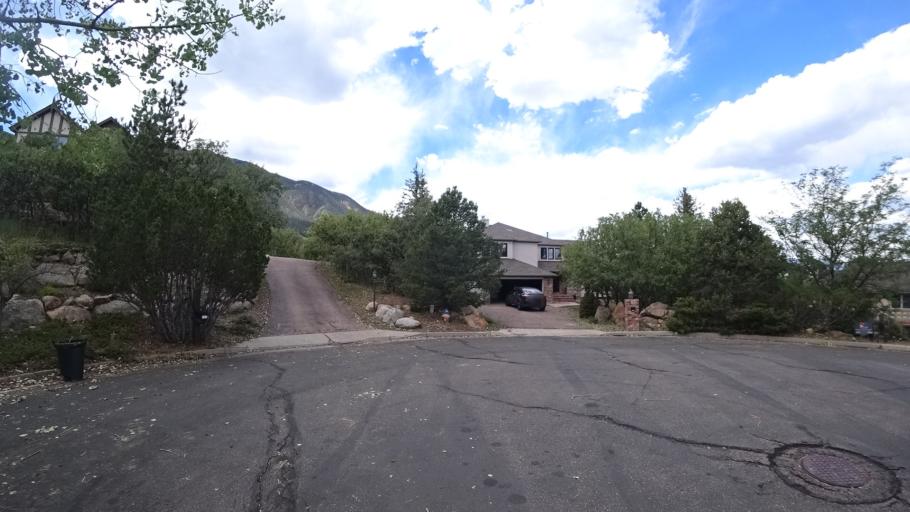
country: US
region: Colorado
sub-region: El Paso County
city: Stratmoor
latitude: 38.7691
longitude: -104.8340
